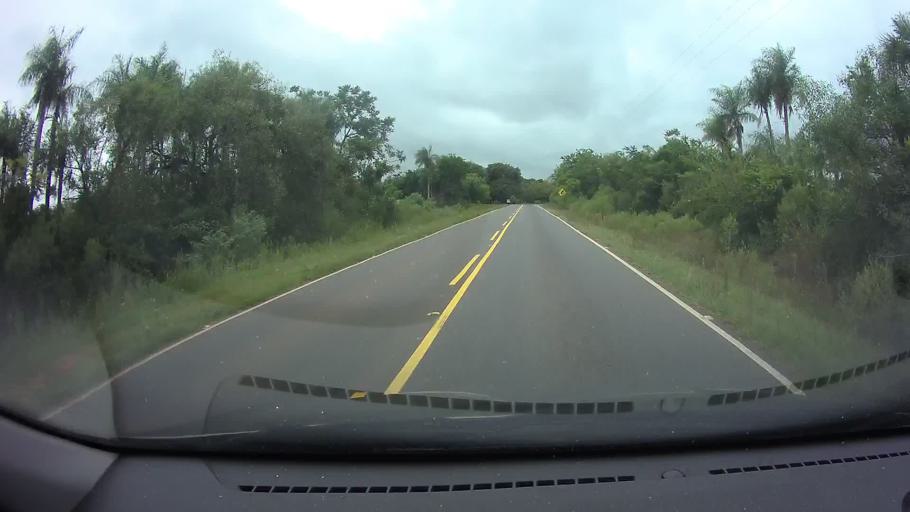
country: PY
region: Paraguari
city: Yaguaron
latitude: -25.7178
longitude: -57.3311
